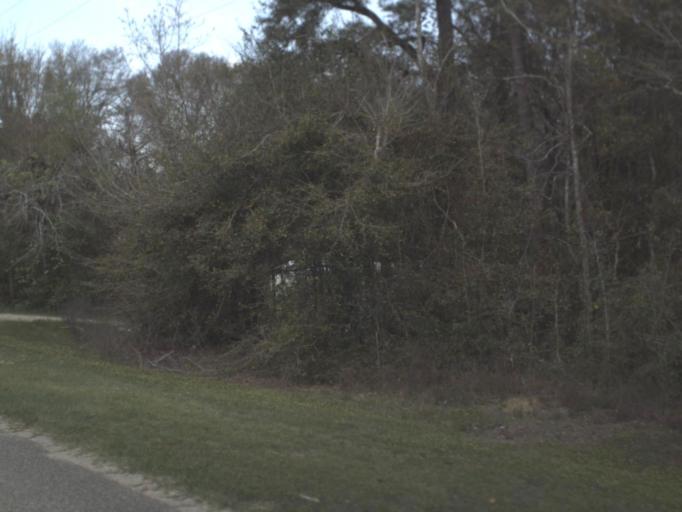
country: US
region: Florida
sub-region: Liberty County
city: Bristol
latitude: 30.4321
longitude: -84.9511
